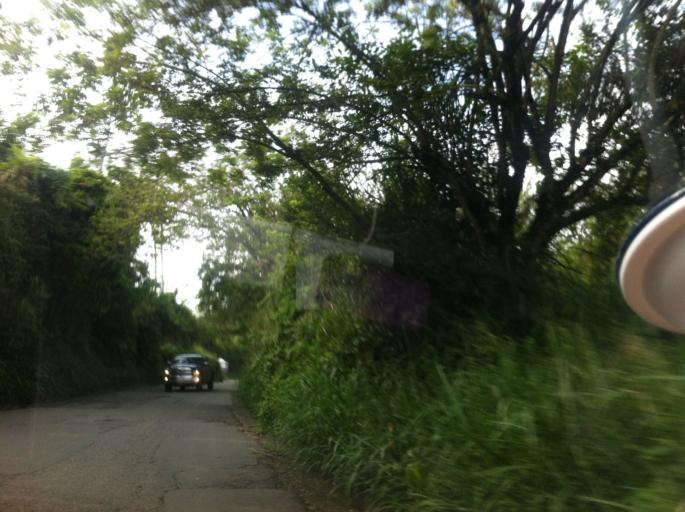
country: CO
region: Quindio
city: La Tebaida
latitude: 4.4668
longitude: -75.8117
